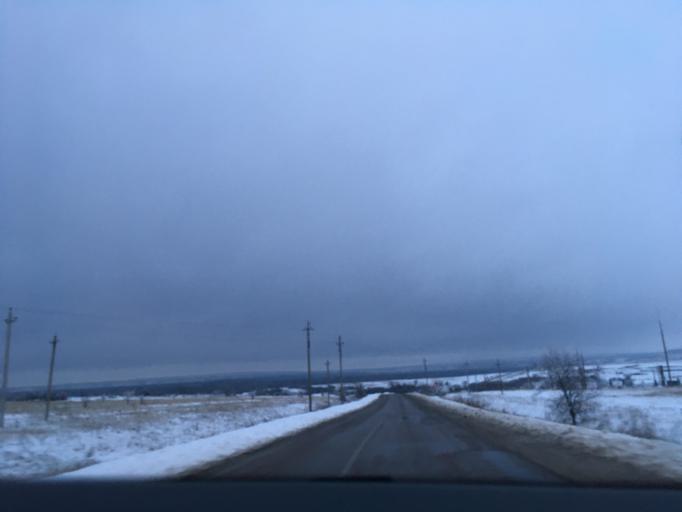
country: RU
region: Voronezj
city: Verkhniy Mamon
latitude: 50.0713
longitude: 40.3101
